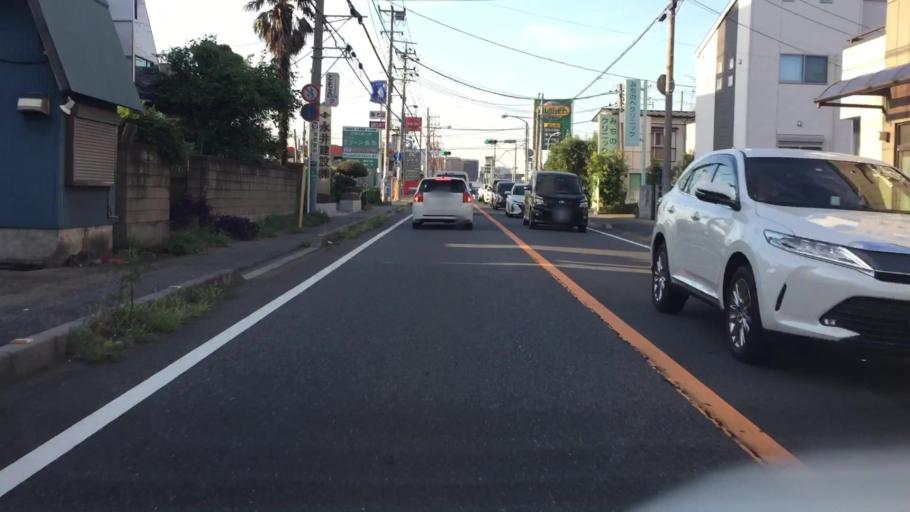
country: JP
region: Chiba
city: Funabashi
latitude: 35.7563
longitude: 139.9986
